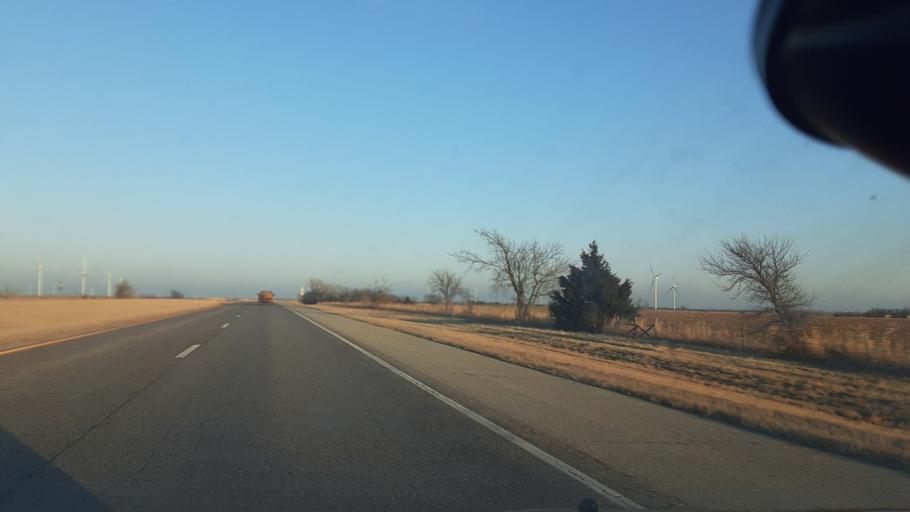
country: US
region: Oklahoma
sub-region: Noble County
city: Perry
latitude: 36.3975
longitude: -97.5202
